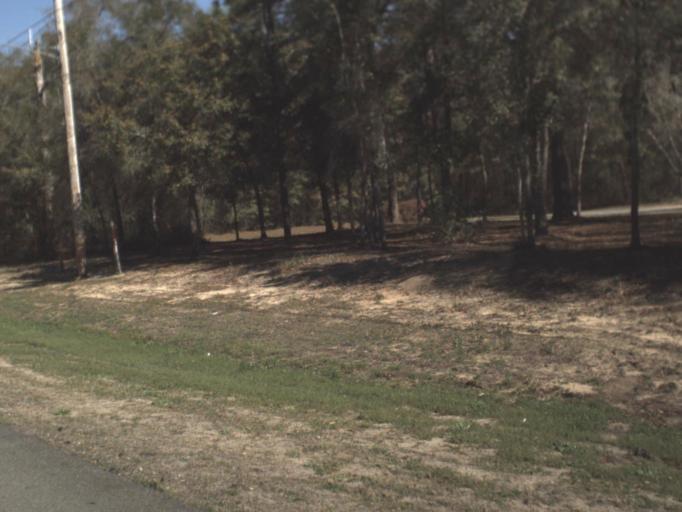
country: US
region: Florida
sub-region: Leon County
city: Tallahassee
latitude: 30.4154
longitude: -84.3454
